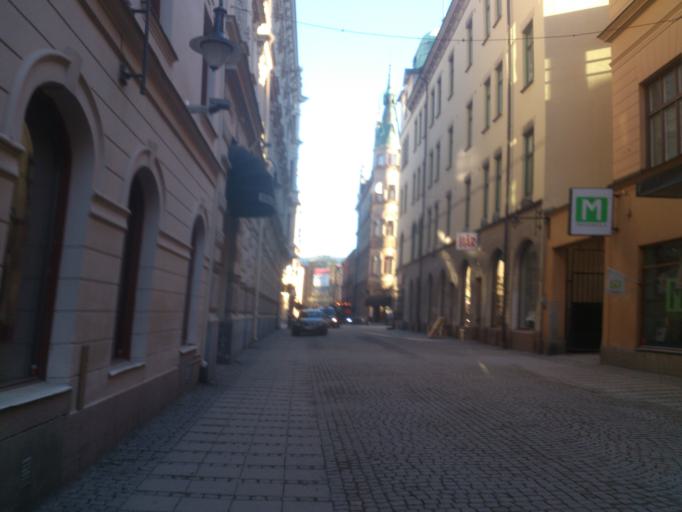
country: SE
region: Vaesternorrland
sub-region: Sundsvalls Kommun
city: Sundsvall
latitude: 62.3900
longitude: 17.3112
